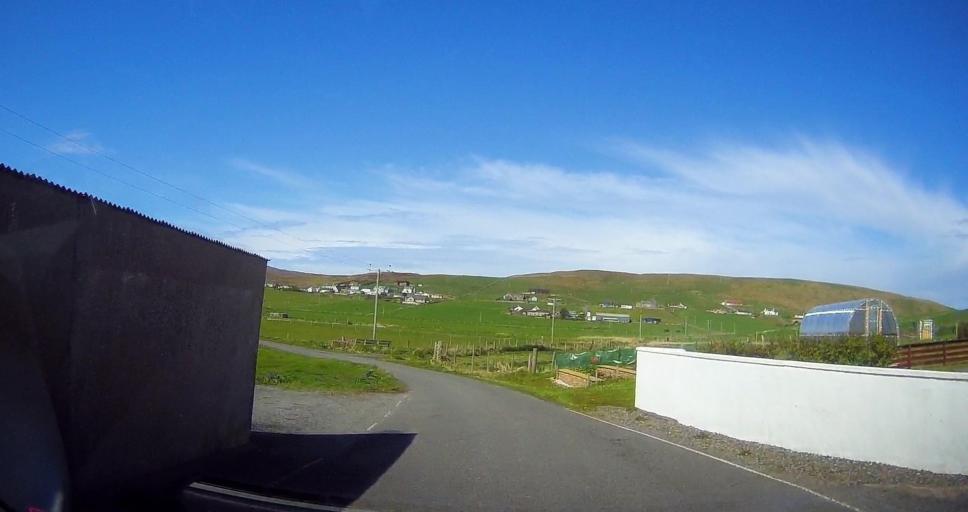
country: GB
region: Scotland
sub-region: Shetland Islands
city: Sandwick
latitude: 60.0476
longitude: -1.2152
